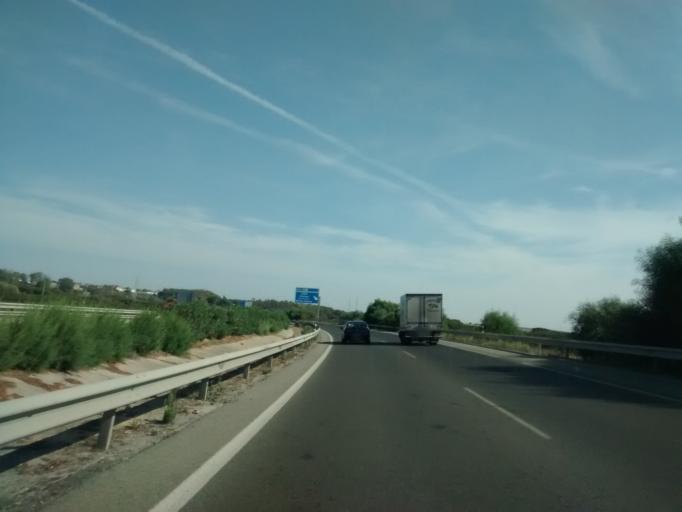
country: ES
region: Andalusia
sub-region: Provincia de Cadiz
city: Chiclana de la Frontera
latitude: 36.4104
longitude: -6.1192
